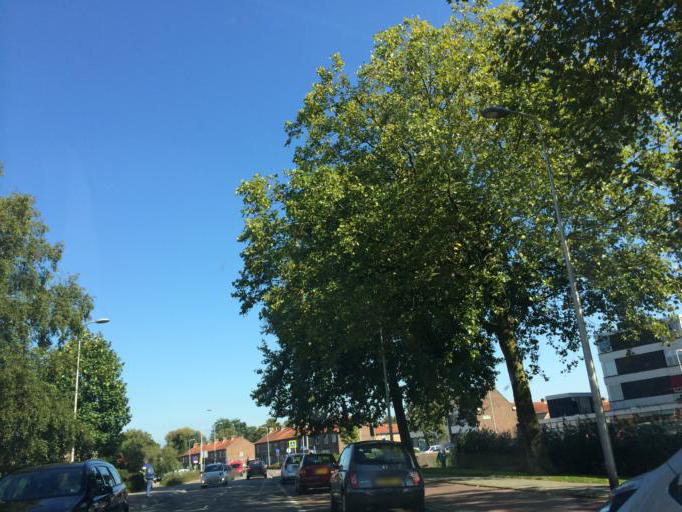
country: NL
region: South Holland
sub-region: Gemeente Capelle aan den IJssel
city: Capelle aan den IJssel
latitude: 51.9249
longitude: 4.5826
